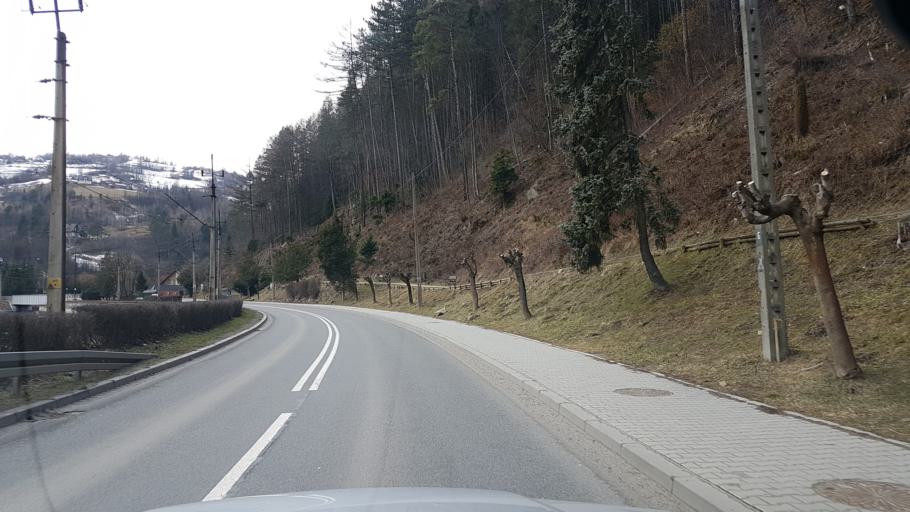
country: PL
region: Lesser Poland Voivodeship
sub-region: Powiat nowosadecki
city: Piwniczna-Zdroj
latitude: 49.4359
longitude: 20.7090
